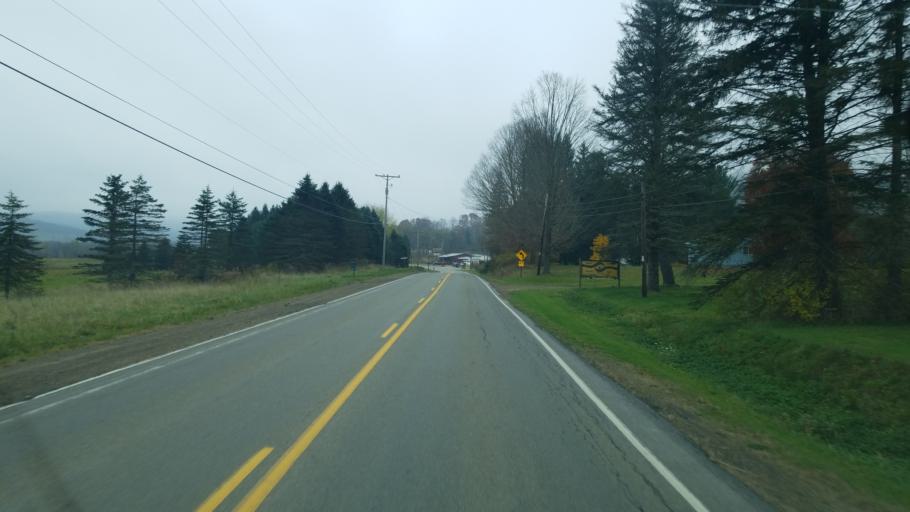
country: US
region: Pennsylvania
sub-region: McKean County
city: Smethport
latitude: 41.8462
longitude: -78.4422
